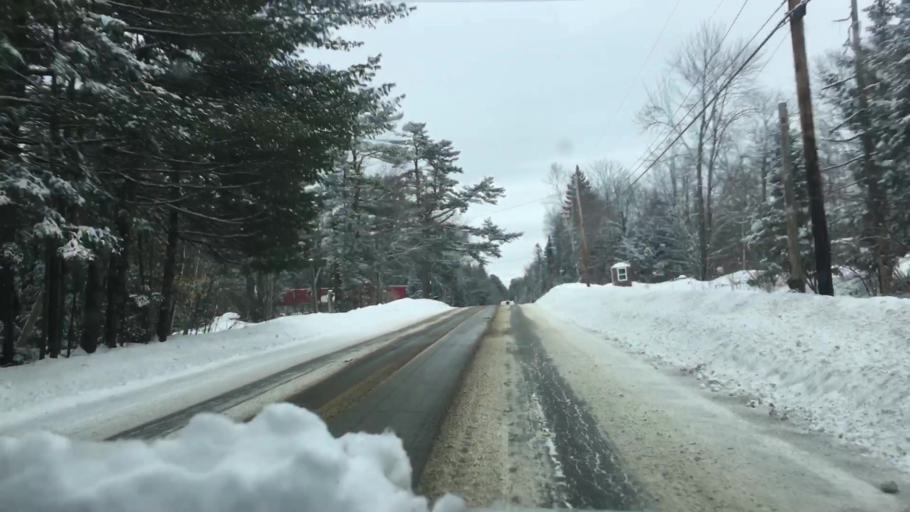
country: US
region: Maine
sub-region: Penobscot County
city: Hudson
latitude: 45.0206
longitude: -68.9117
